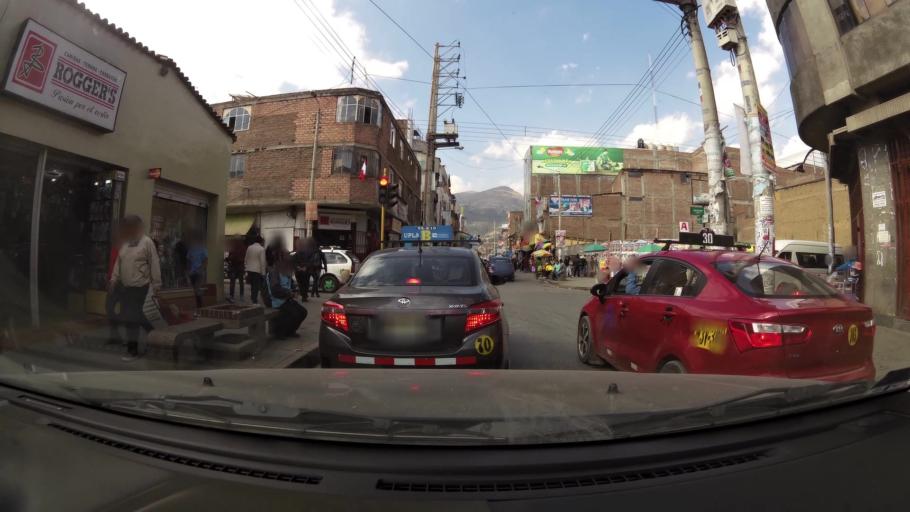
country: PE
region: Junin
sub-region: Provincia de Huancayo
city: Huancayo
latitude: -12.0720
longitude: -75.2070
